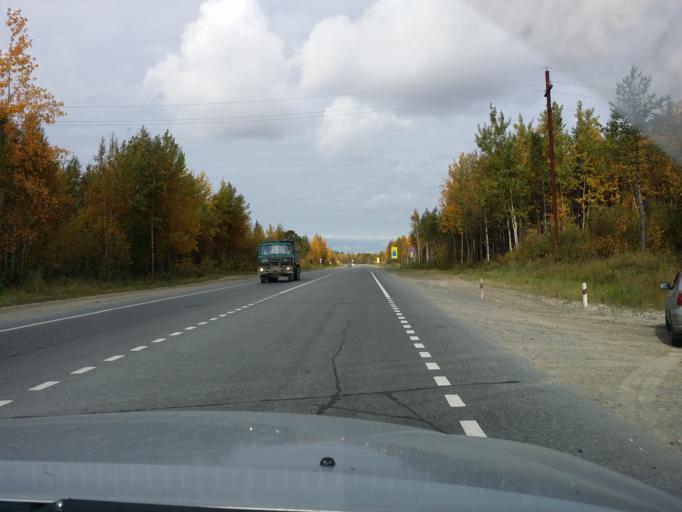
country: RU
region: Khanty-Mansiyskiy Avtonomnyy Okrug
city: Megion
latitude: 61.1067
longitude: 76.0419
